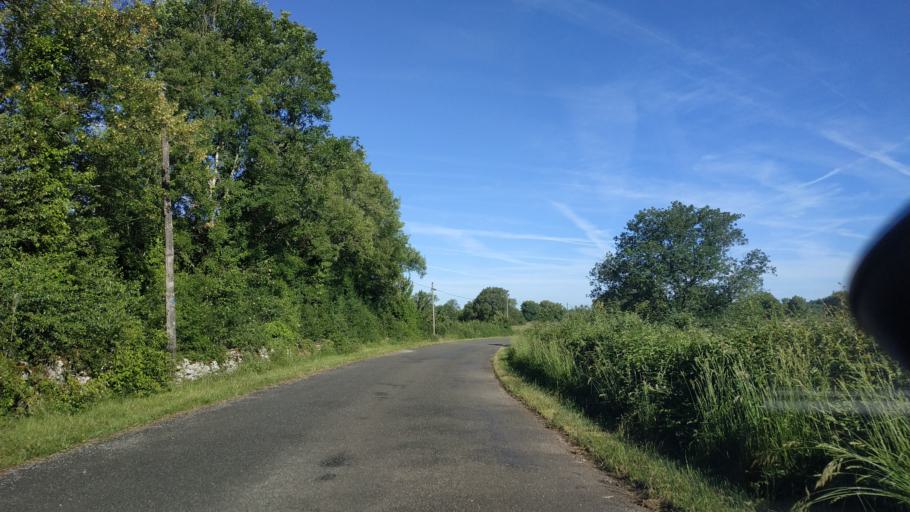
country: FR
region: Midi-Pyrenees
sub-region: Departement du Lot
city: Lacapelle-Marival
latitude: 44.6311
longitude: 1.8675
